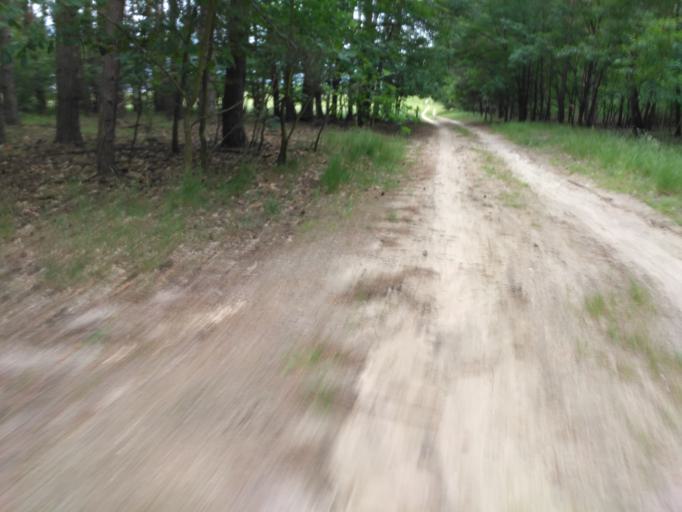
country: DE
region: Brandenburg
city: Hohenleipisch
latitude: 51.5004
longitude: 13.5245
